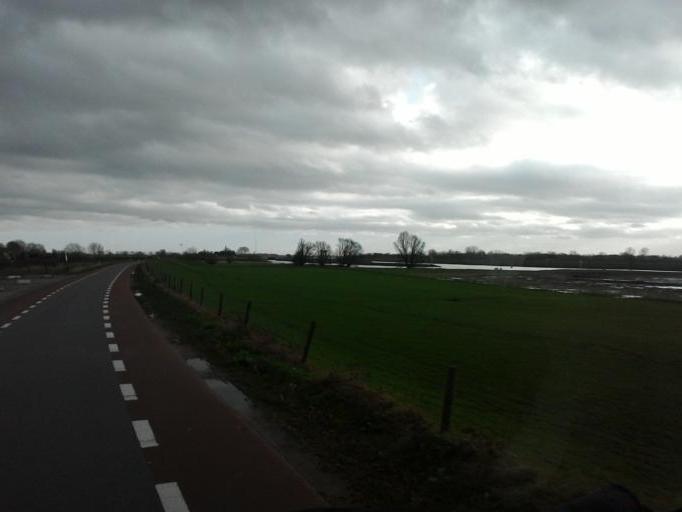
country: NL
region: Utrecht
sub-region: Gemeente Vianen
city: Vianen
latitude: 52.0028
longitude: 5.1227
